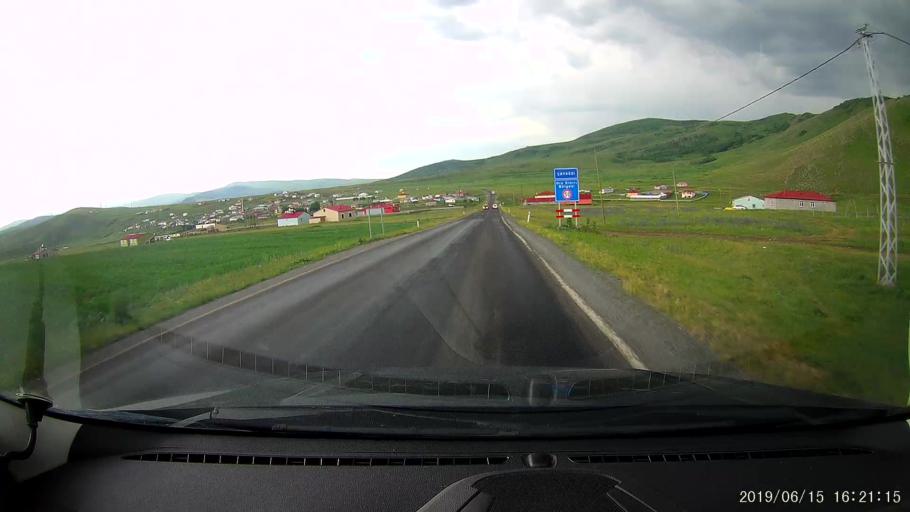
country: TR
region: Ardahan
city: Hanak
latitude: 41.2007
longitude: 42.8460
